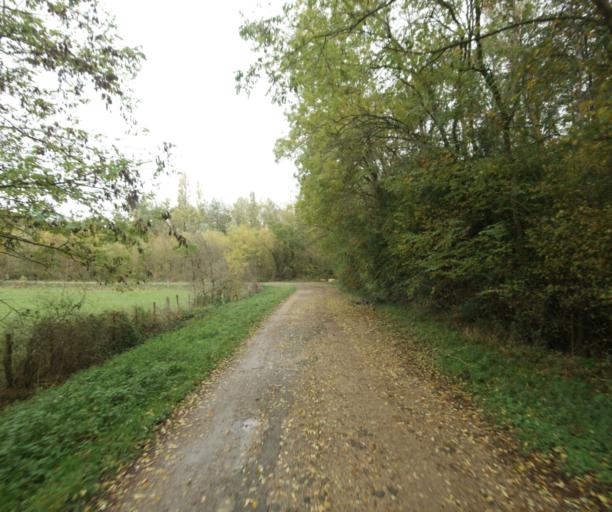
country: FR
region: Rhone-Alpes
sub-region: Departement de l'Ain
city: Pont-de-Vaux
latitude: 46.4599
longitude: 4.8972
